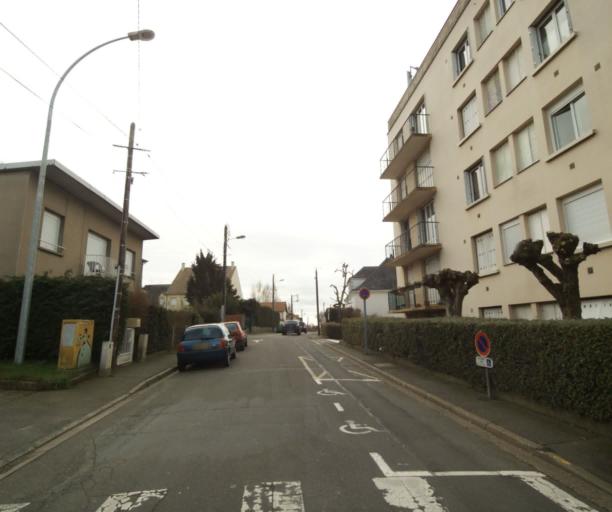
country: FR
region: Pays de la Loire
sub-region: Departement de la Sarthe
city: Le Mans
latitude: 48.0079
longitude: 0.2137
